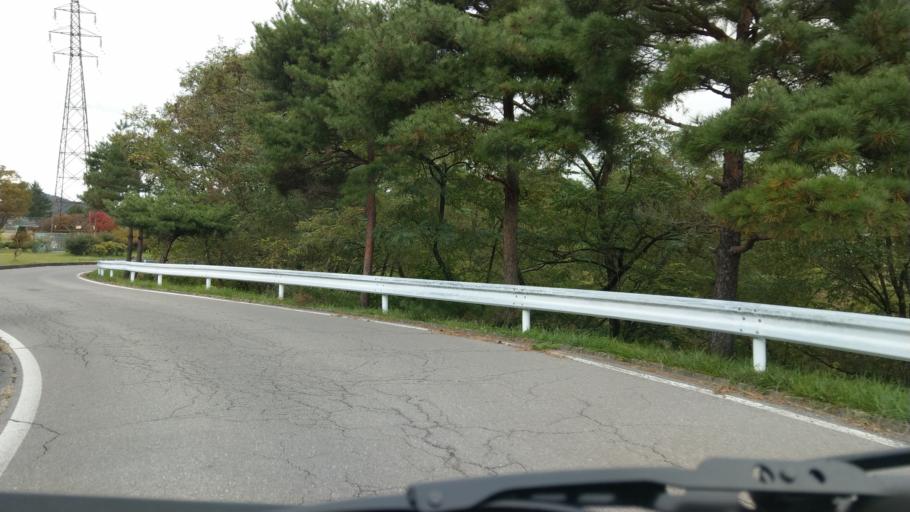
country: JP
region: Nagano
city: Komoro
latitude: 36.3107
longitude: 138.4370
